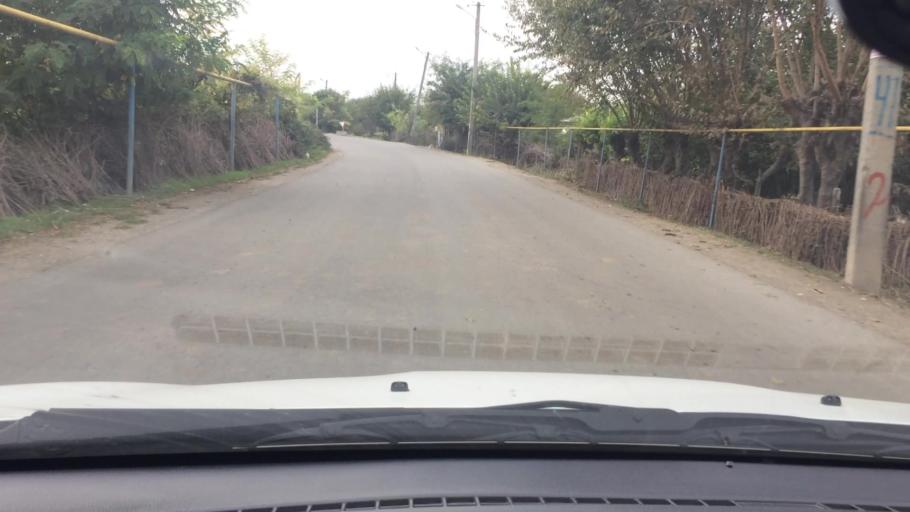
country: AM
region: Tavush
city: Berdavan
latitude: 41.3526
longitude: 44.9677
